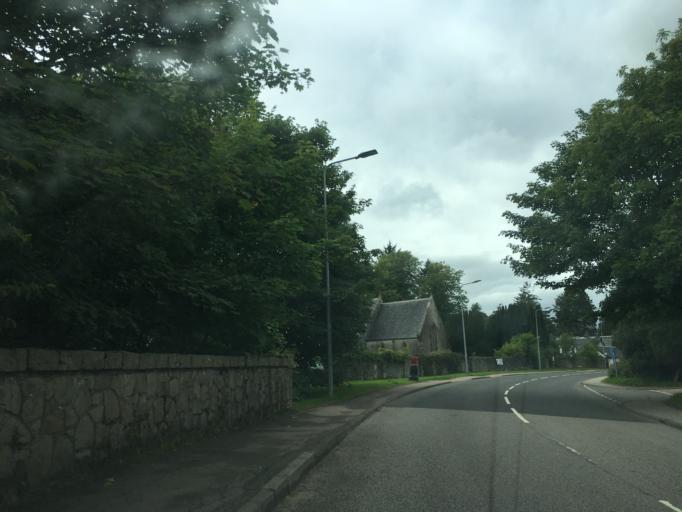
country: GB
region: Scotland
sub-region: Argyll and Bute
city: Lochgilphead
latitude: 56.0397
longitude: -5.4359
